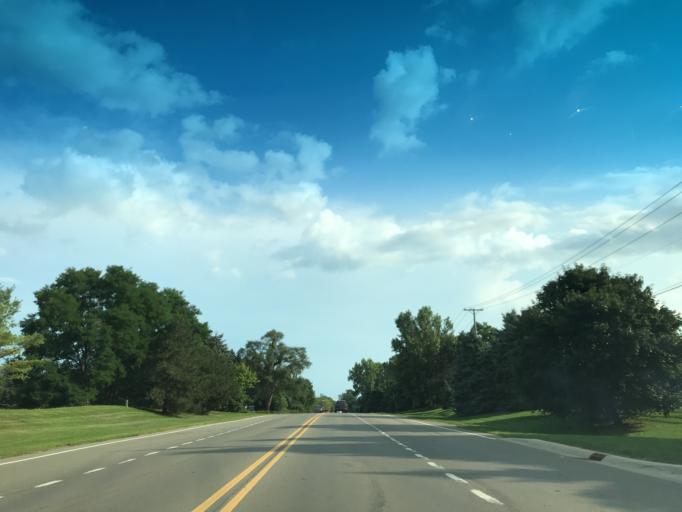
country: US
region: Michigan
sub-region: Oakland County
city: Milford
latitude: 42.5542
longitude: -83.6181
